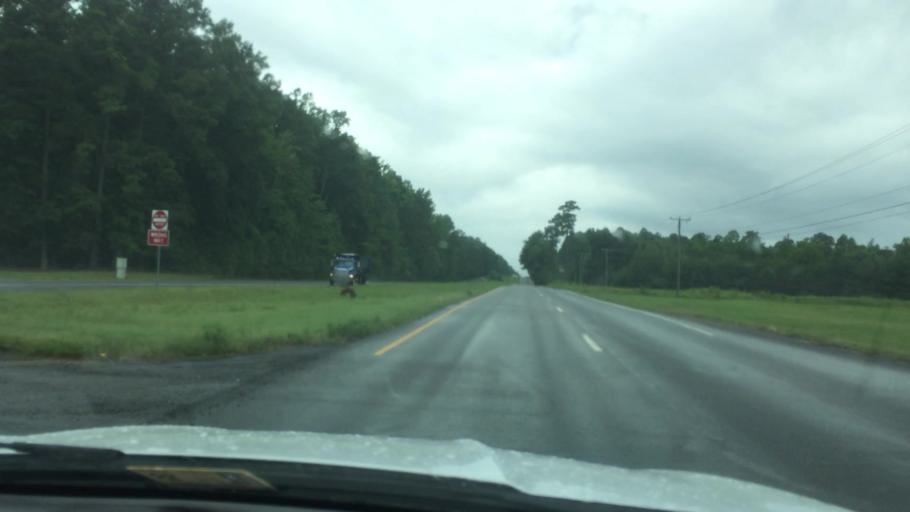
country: US
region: Virginia
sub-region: King William County
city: West Point
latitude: 37.5066
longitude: -76.8593
